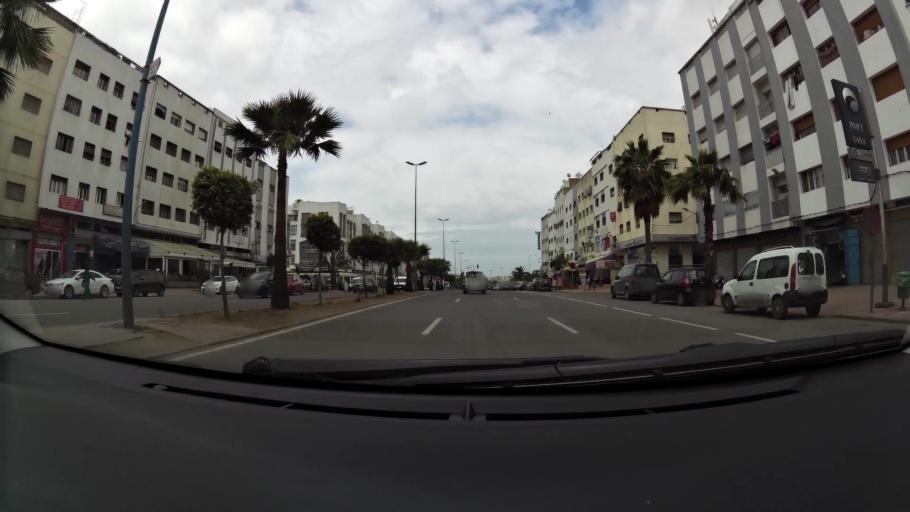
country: MA
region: Grand Casablanca
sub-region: Casablanca
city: Casablanca
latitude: 33.5709
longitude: -7.5612
